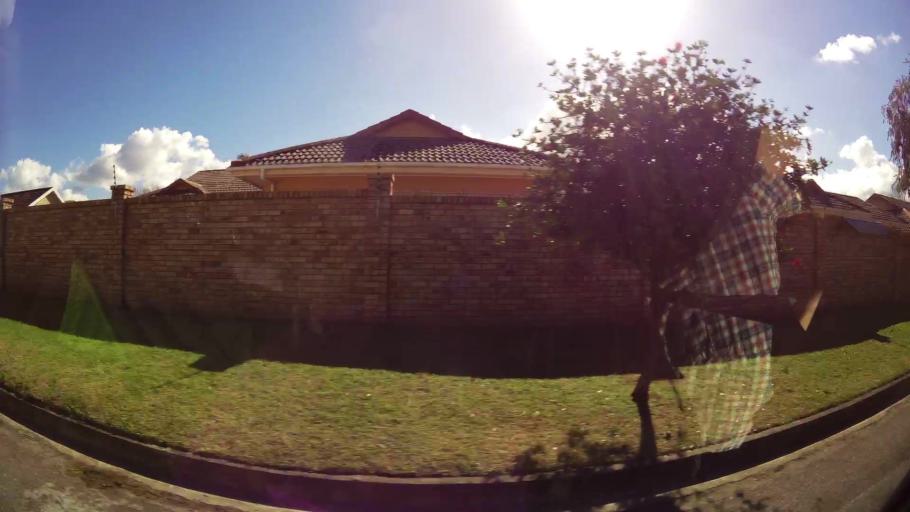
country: ZA
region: Western Cape
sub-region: Eden District Municipality
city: George
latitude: -33.9577
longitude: 22.4345
